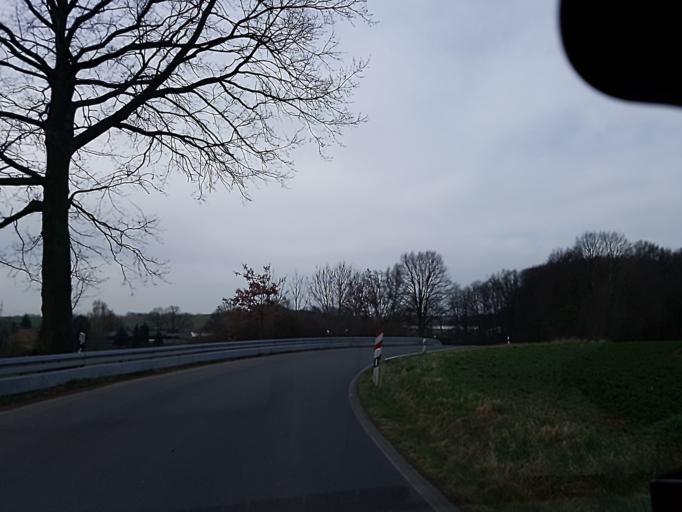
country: DE
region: Saxony
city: Grossweitzschen
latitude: 51.1472
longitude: 13.0351
